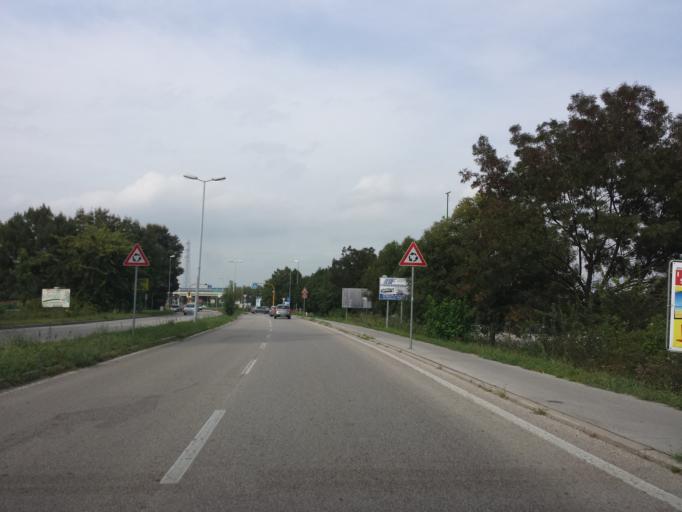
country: IT
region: Veneto
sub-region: Provincia di Padova
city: Mejaniga
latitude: 45.4337
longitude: 11.8977
